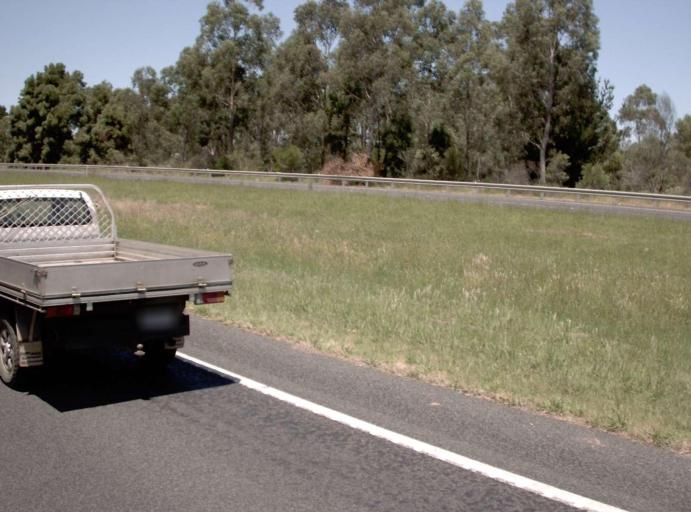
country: AU
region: Victoria
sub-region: Baw Baw
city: Warragul
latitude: -38.1125
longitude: 145.8607
